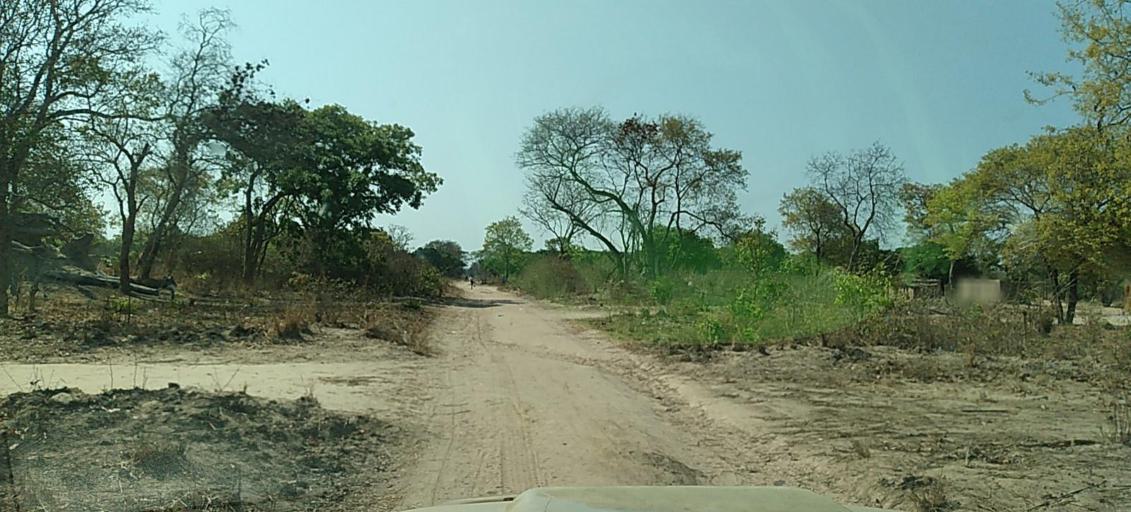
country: ZM
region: North-Western
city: Kalengwa
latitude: -13.3543
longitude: 24.8582
